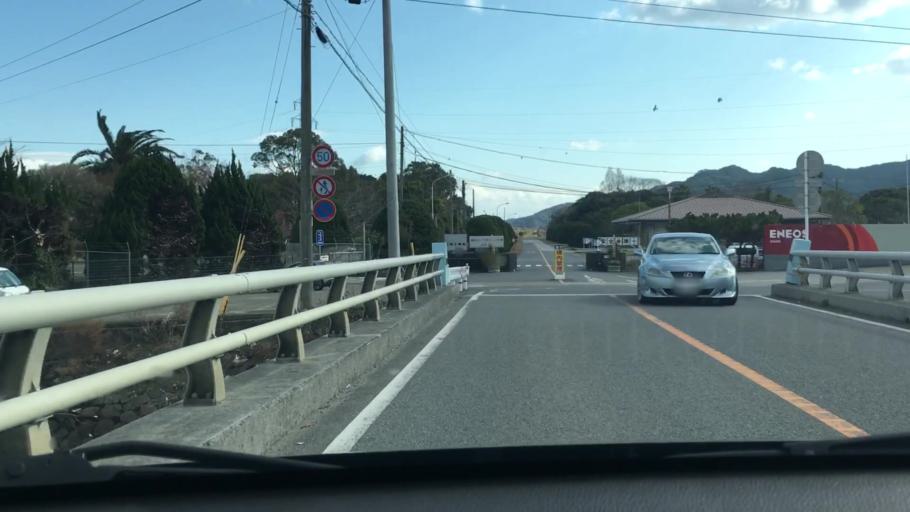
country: JP
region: Oita
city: Saiki
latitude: 32.9688
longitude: 131.9157
